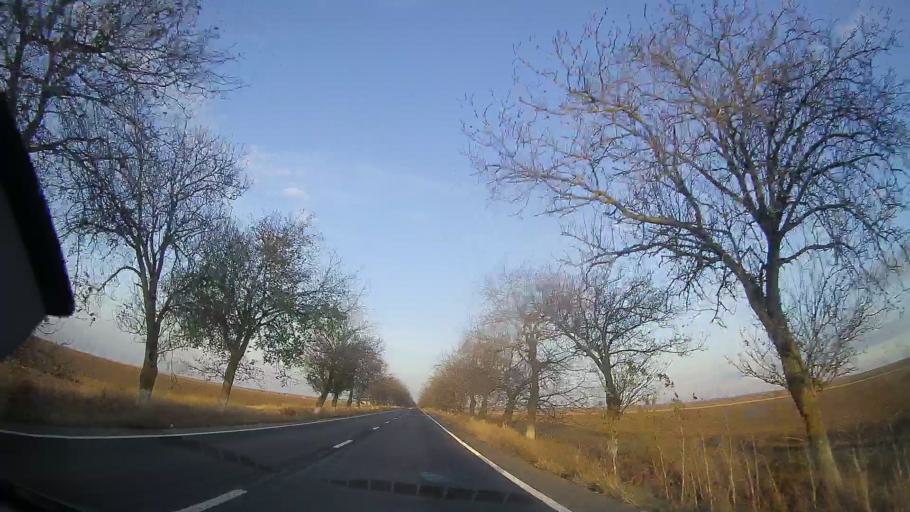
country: RO
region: Constanta
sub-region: Comuna Comana
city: Comana
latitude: 43.8804
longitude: 28.2911
